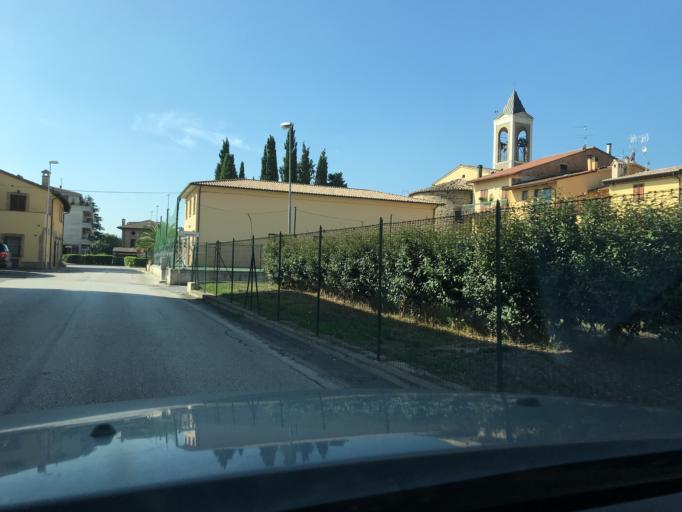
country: IT
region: Umbria
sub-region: Provincia di Perugia
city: Ospedalicchio
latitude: 43.0799
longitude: 12.5047
